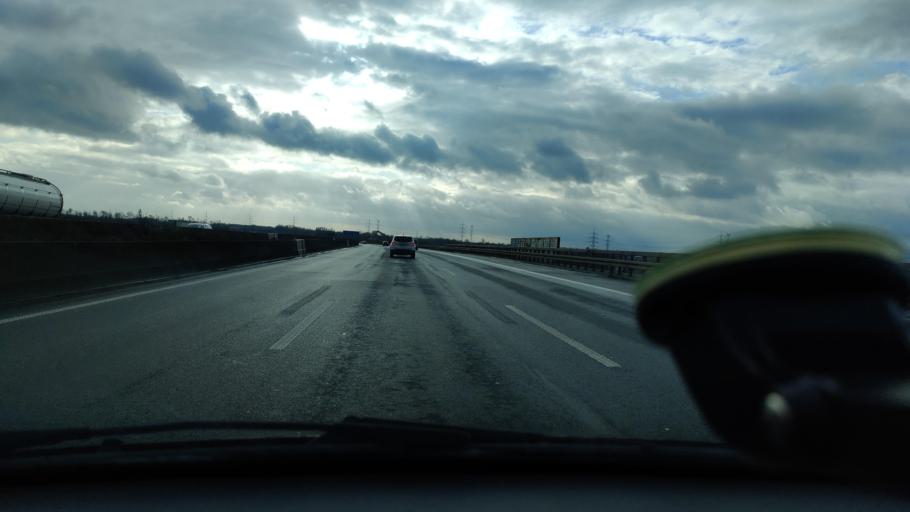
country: DE
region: North Rhine-Westphalia
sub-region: Regierungsbezirk Dusseldorf
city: Kaarst
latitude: 51.2521
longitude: 6.6386
